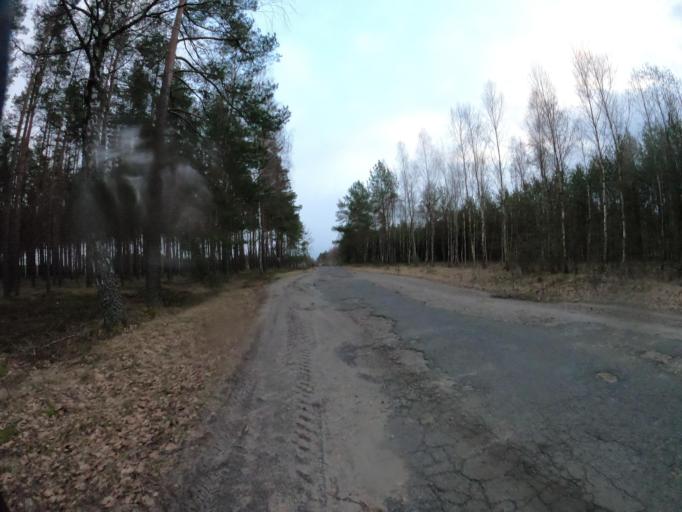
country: PL
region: West Pomeranian Voivodeship
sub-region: Powiat szczecinecki
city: Borne Sulinowo
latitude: 53.5503
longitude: 16.5811
